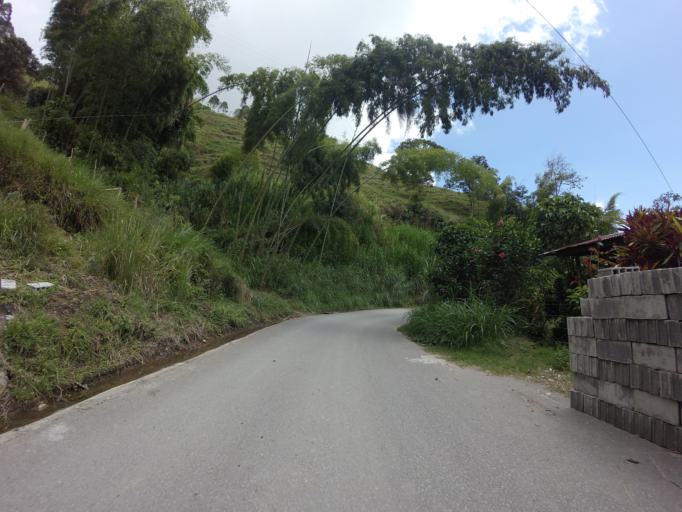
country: CO
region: Caldas
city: Marquetalia
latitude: 5.2954
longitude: -75.0871
